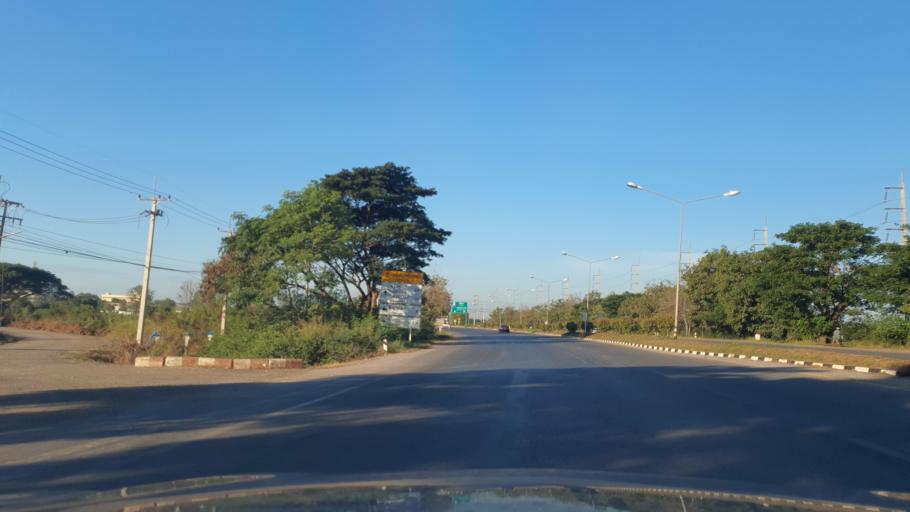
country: TH
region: Phitsanulok
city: Phitsanulok
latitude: 16.8652
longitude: 100.2209
